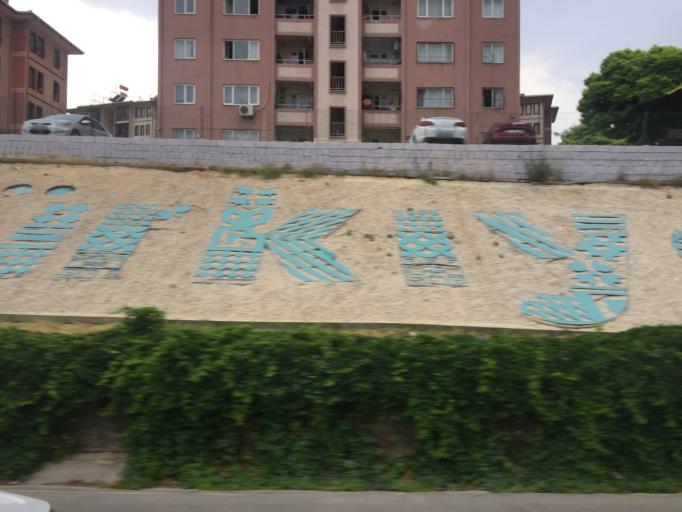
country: TR
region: Gaziantep
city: Gaziantep
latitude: 37.0434
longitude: 37.4247
